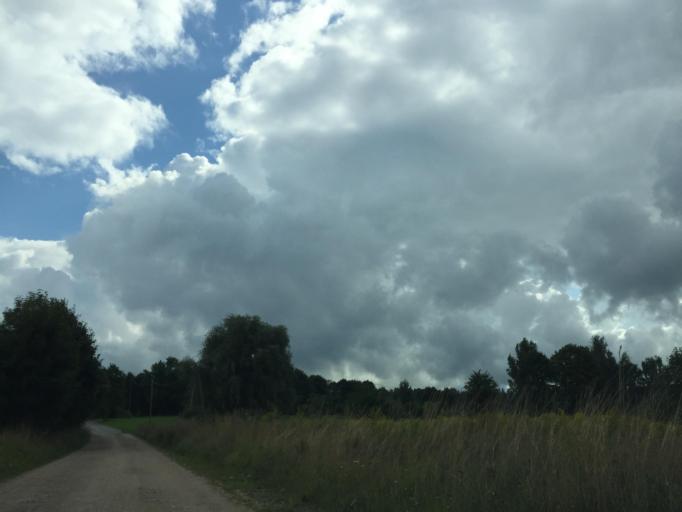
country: LV
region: Raunas
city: Rauna
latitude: 57.3382
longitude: 25.4856
